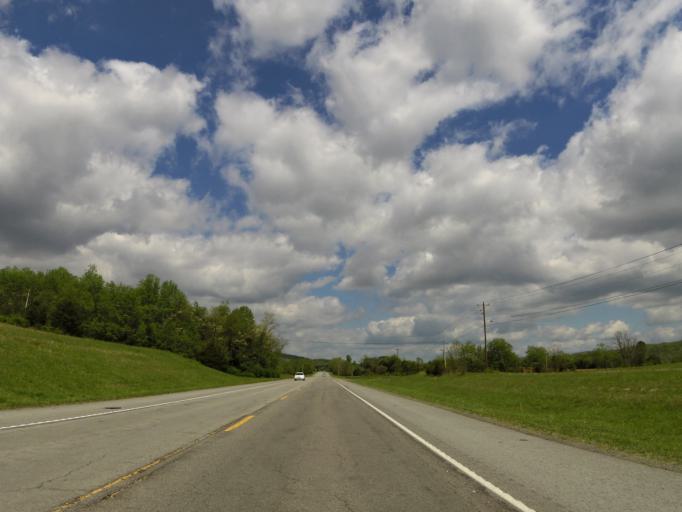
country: US
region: Tennessee
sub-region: Campbell County
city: Fincastle
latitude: 36.4544
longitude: -83.9104
